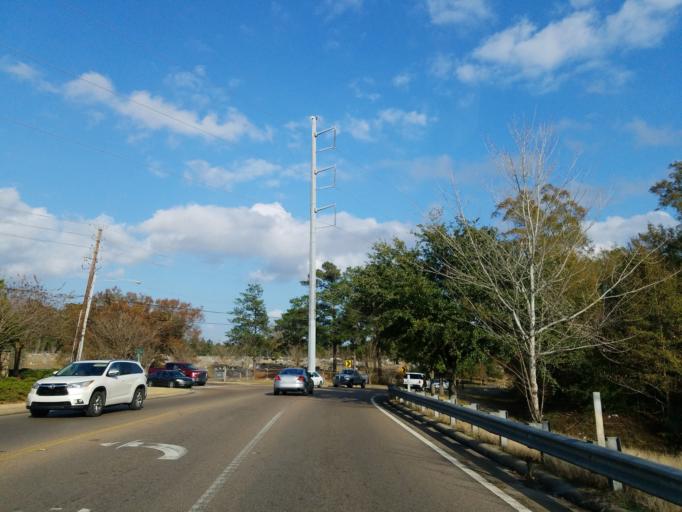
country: US
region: Mississippi
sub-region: Lamar County
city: Arnold Line
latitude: 31.3357
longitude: -89.3443
